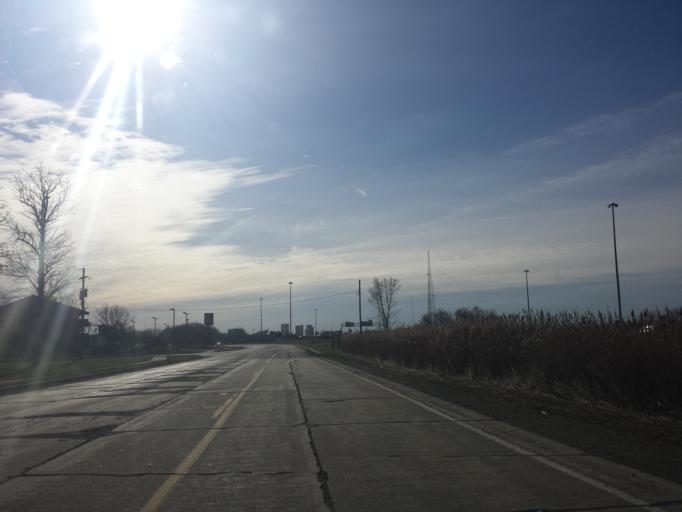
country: US
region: Michigan
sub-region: Oakland County
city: Bingham Farms
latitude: 42.4944
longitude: -83.2909
